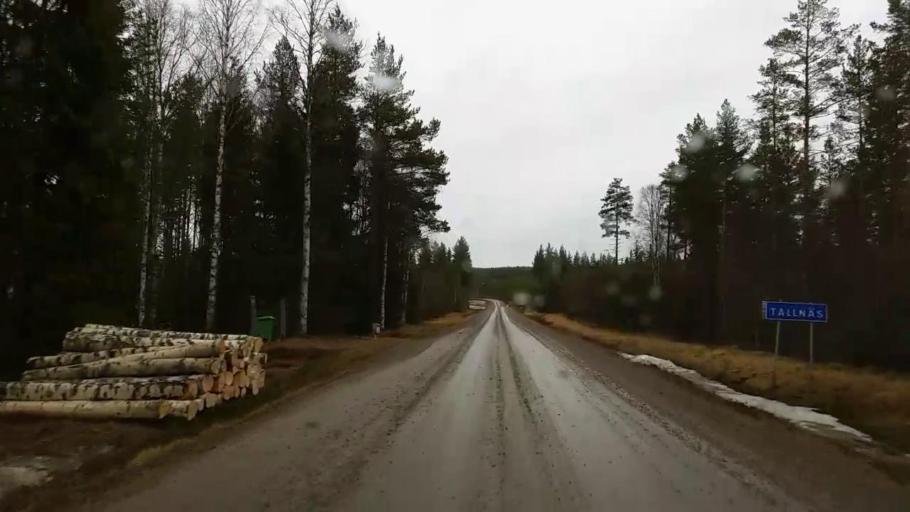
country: SE
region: Gaevleborg
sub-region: Ljusdals Kommun
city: Farila
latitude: 62.1175
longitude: 15.6859
